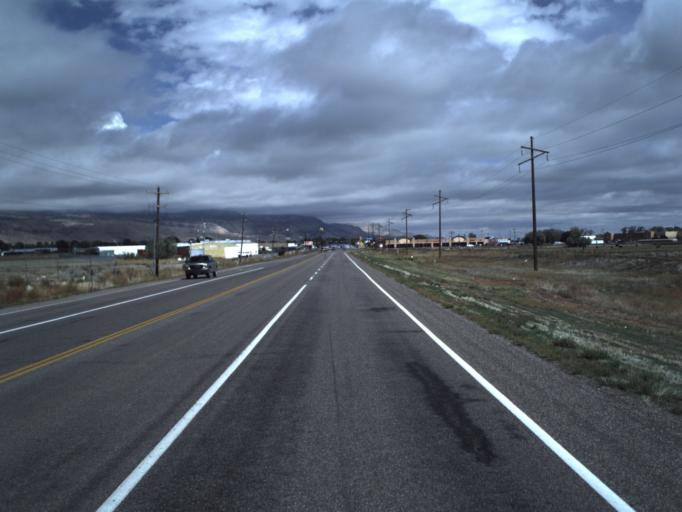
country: US
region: Utah
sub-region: Sevier County
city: Richfield
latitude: 38.7423
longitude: -112.0915
